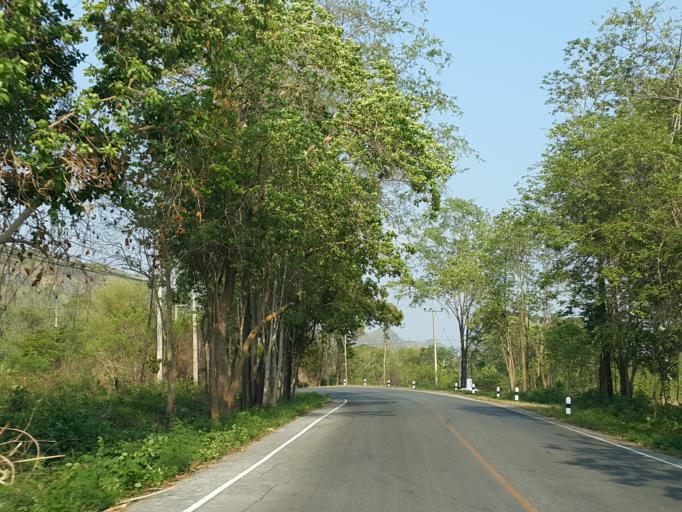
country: TH
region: Kanchanaburi
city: Sai Yok
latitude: 14.2200
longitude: 99.1691
